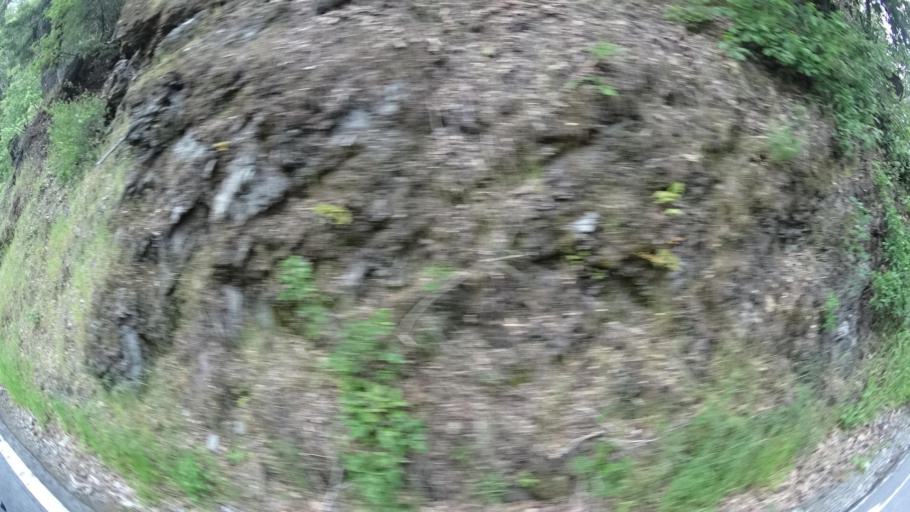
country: US
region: California
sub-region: Humboldt County
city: Willow Creek
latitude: 41.1955
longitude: -123.7226
